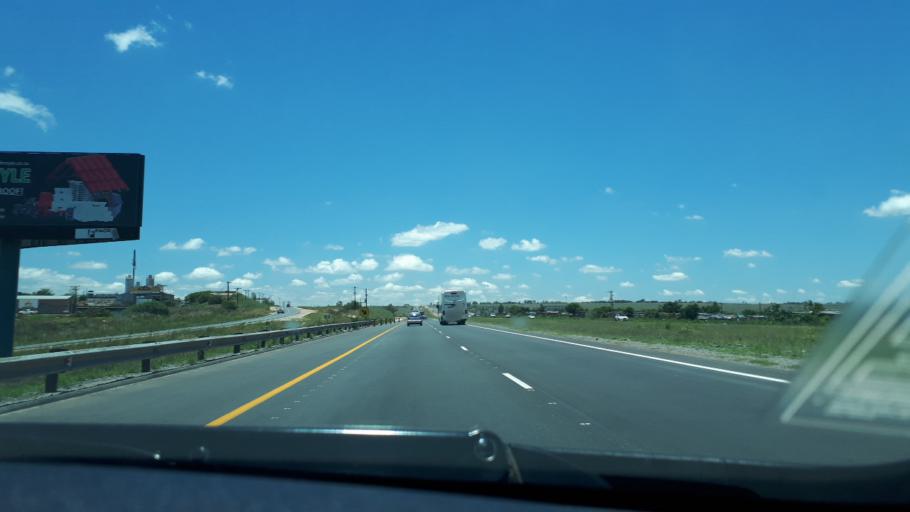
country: ZA
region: Gauteng
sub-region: City of Johannesburg Metropolitan Municipality
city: Diepsloot
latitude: -25.9257
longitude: 28.0034
